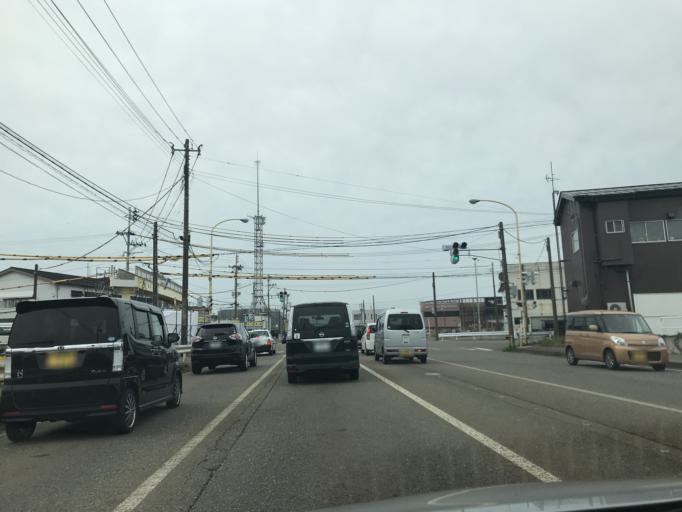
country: JP
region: Niigata
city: Nagaoka
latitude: 37.4262
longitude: 138.8396
